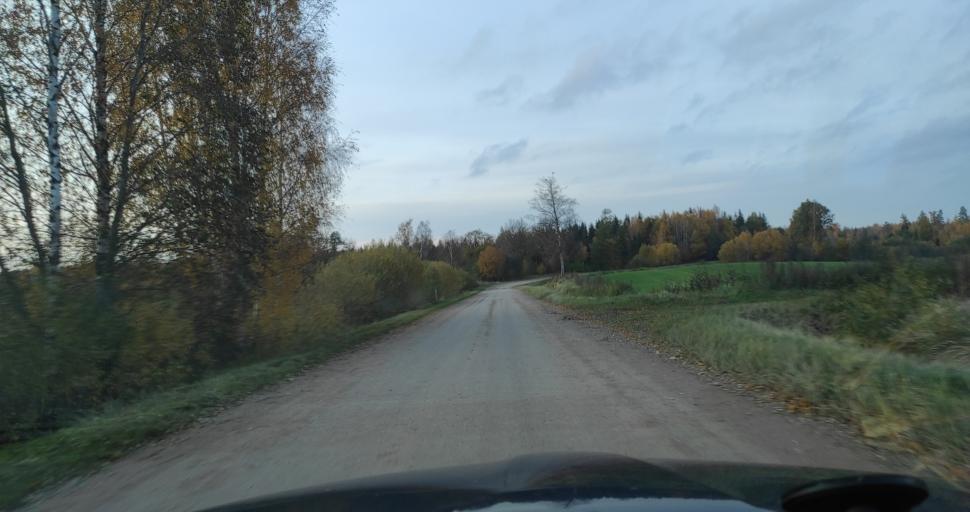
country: LV
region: Aizpute
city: Aizpute
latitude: 56.6679
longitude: 21.7939
